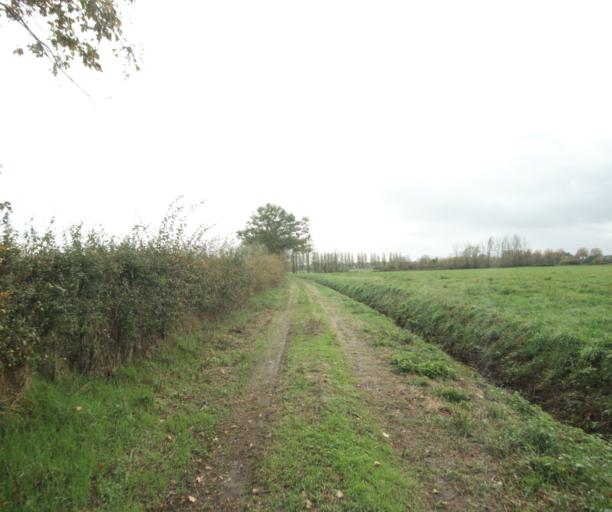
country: FR
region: Rhone-Alpes
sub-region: Departement de l'Ain
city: Pont-de-Vaux
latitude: 46.4545
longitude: 4.8902
